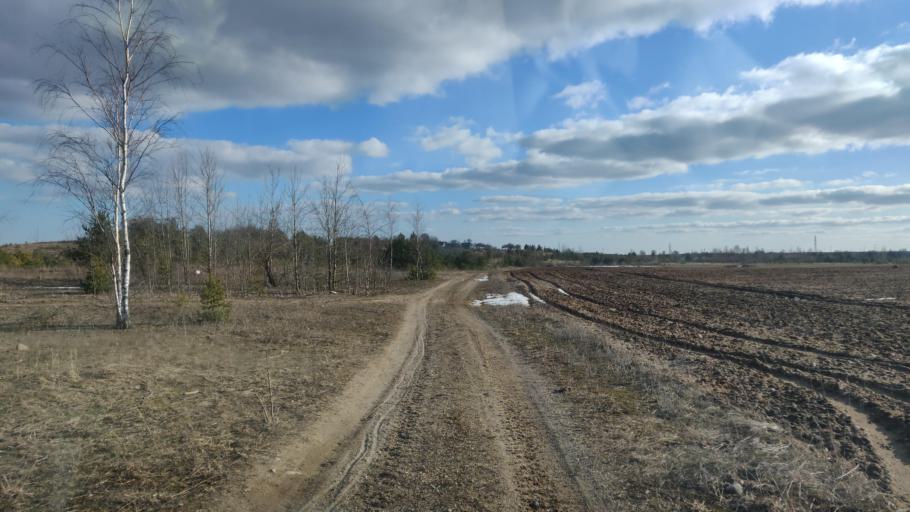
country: LT
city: Lentvaris
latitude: 54.6172
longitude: 24.9973
